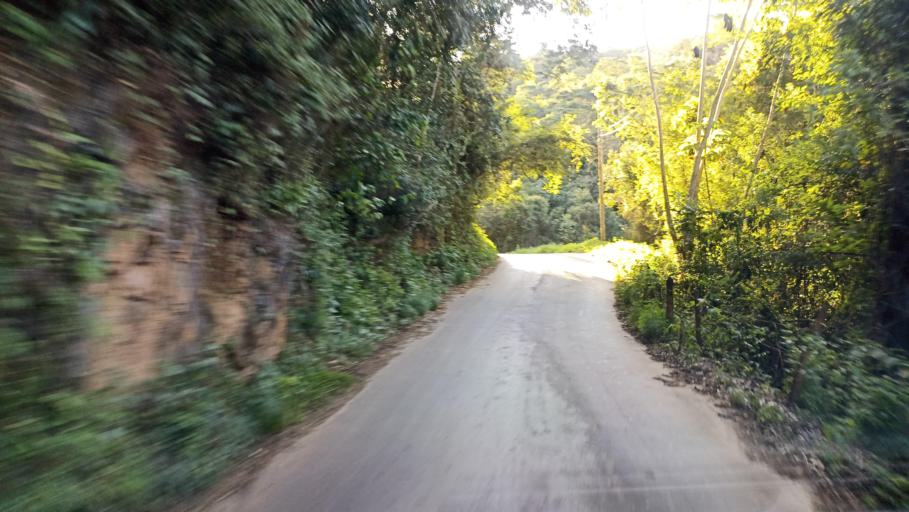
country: BR
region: Minas Gerais
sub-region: Ouro Preto
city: Ouro Preto
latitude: -20.3120
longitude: -43.6099
